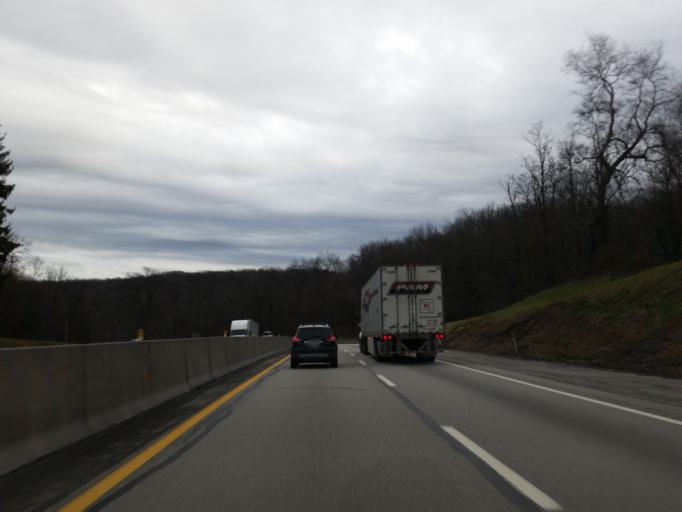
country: US
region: Pennsylvania
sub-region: Somerset County
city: Somerset
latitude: 40.0618
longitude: -79.1407
